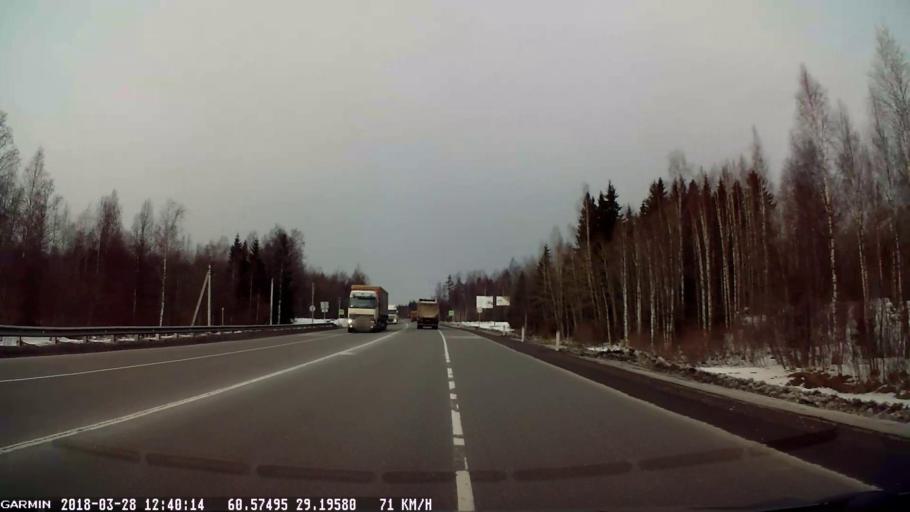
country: RU
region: Leningrad
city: Veshchevo
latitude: 60.5751
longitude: 29.1956
